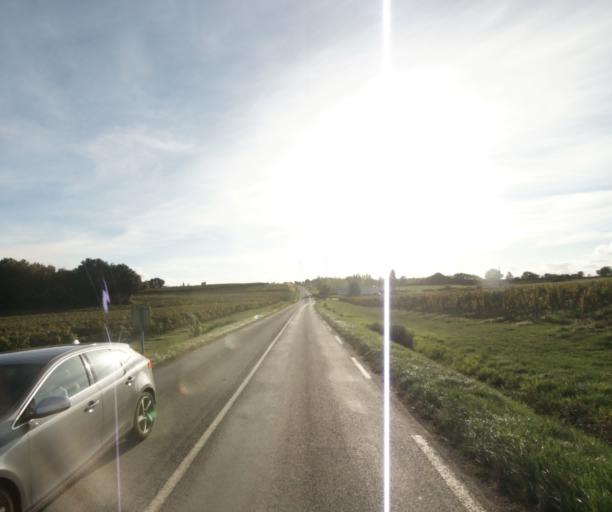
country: FR
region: Midi-Pyrenees
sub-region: Departement du Gers
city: Gondrin
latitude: 43.8967
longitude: 0.2486
